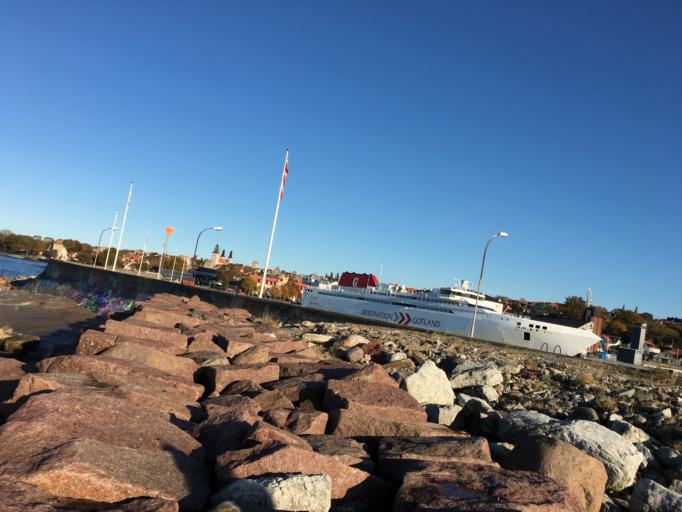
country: SE
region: Gotland
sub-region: Gotland
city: Visby
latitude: 57.6377
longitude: 18.2828
